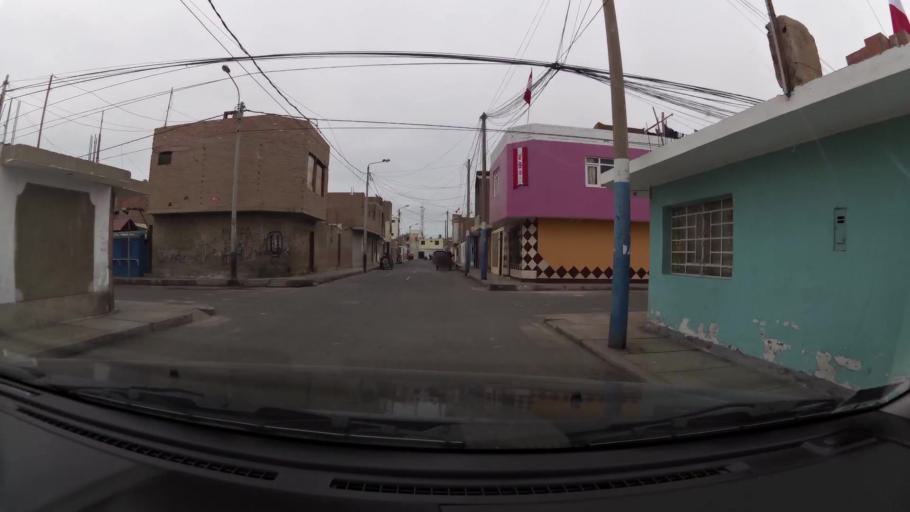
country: PE
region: Ica
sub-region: Provincia de Pisco
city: Pisco
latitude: -13.7126
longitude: -76.1993
